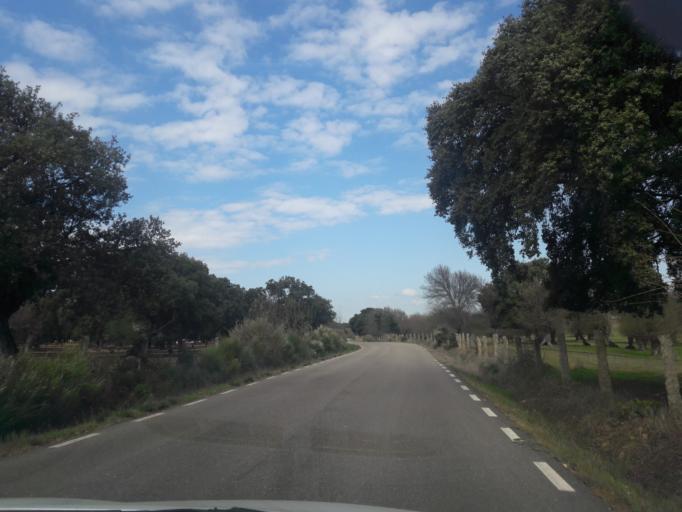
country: ES
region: Castille and Leon
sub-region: Provincia de Salamanca
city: Zamarra
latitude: 40.5546
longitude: -6.4471
